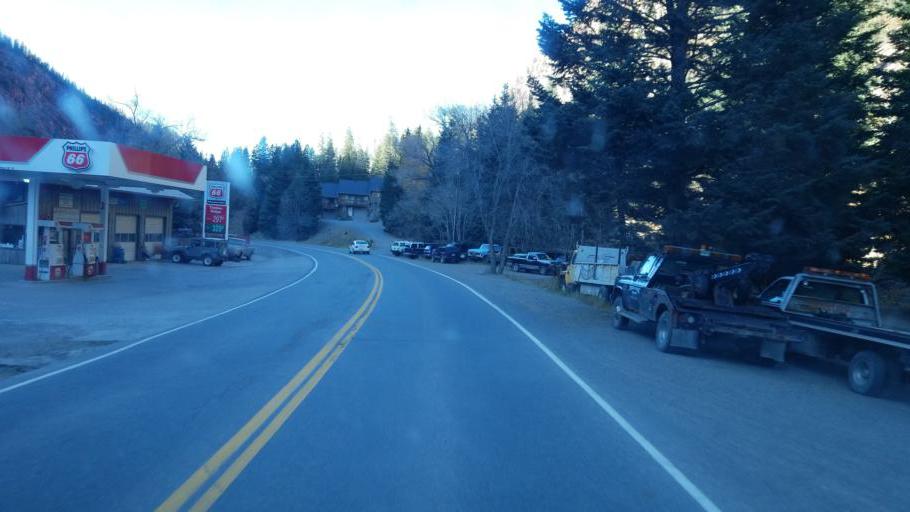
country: US
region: Colorado
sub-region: Ouray County
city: Ouray
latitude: 38.0341
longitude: -107.6748
